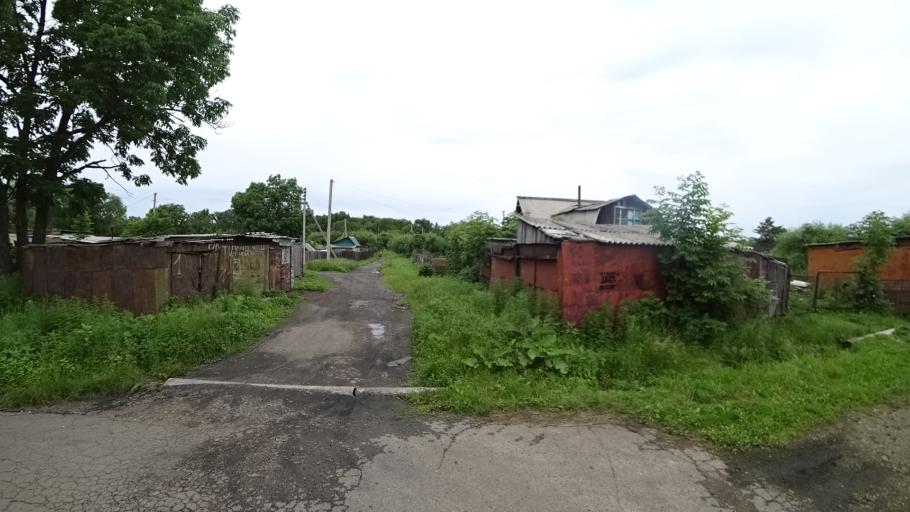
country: RU
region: Primorskiy
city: Novosysoyevka
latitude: 44.1822
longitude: 133.3521
